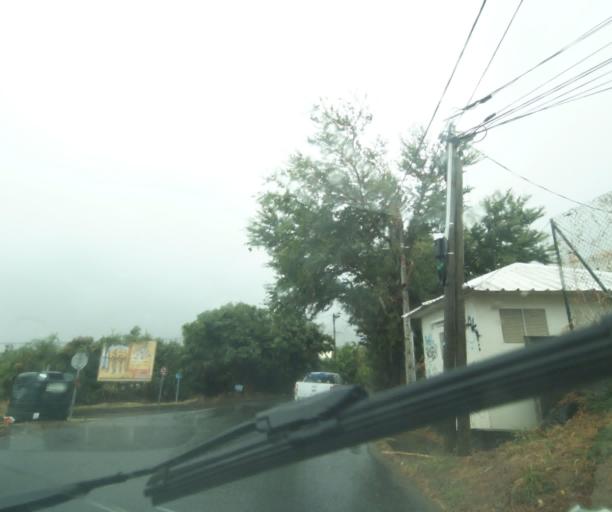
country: RE
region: Reunion
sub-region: Reunion
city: La Possession
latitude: -20.9769
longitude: 55.3286
